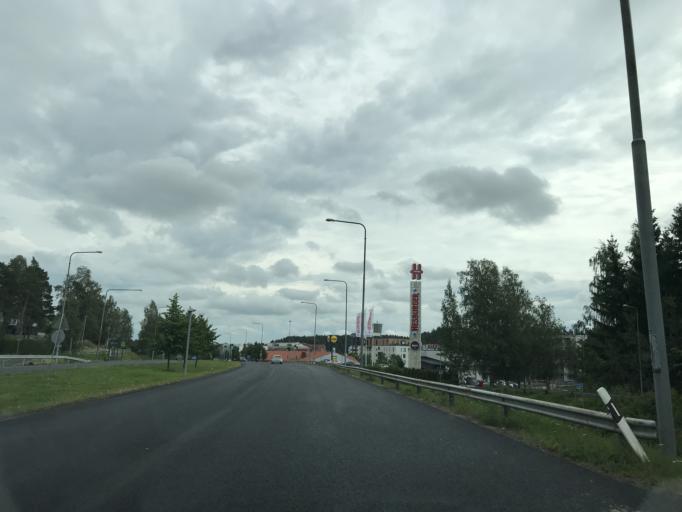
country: FI
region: Varsinais-Suomi
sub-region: Turku
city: Kaarina
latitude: 60.4095
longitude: 22.3601
